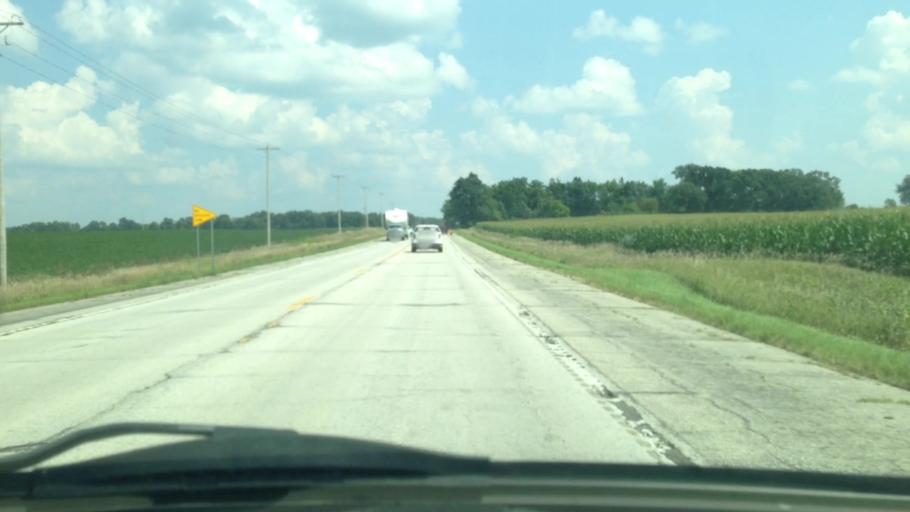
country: US
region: Minnesota
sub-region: Fillmore County
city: Spring Valley
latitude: 43.7110
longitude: -92.4379
